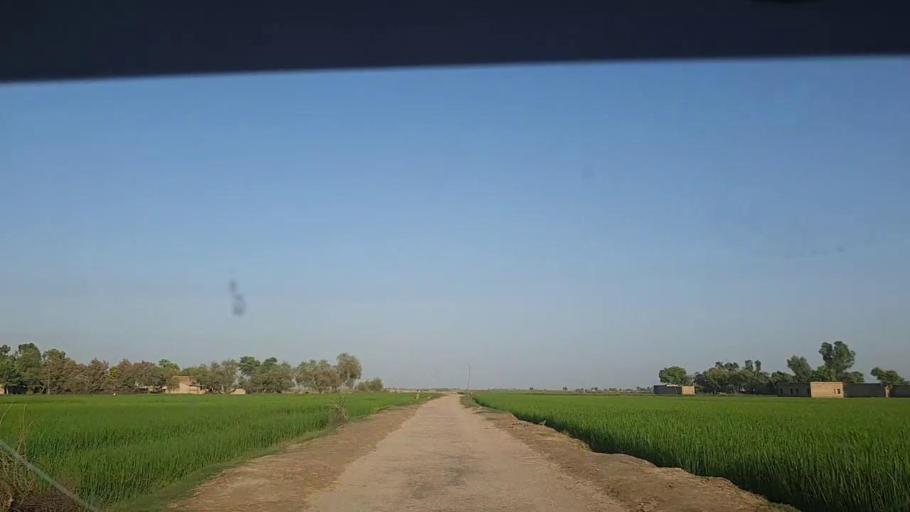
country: PK
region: Sindh
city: Thul
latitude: 28.2120
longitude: 68.8843
